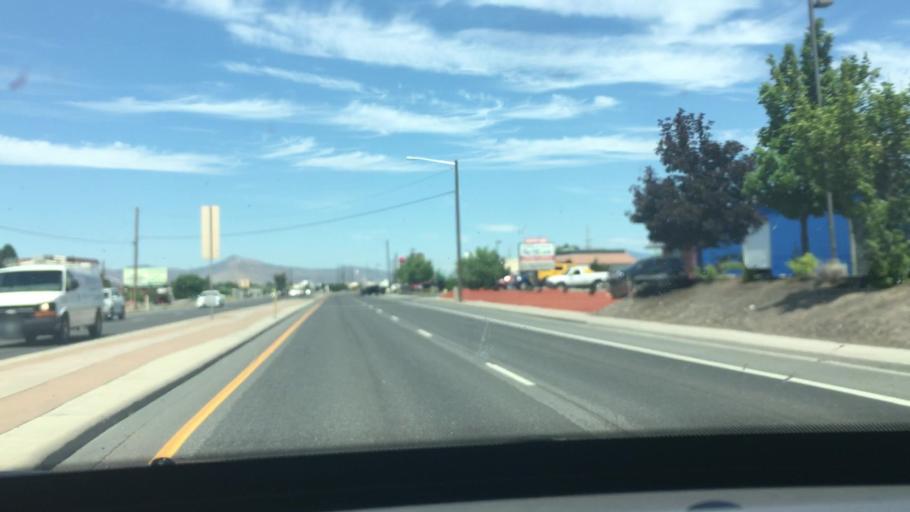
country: US
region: Oregon
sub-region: Deschutes County
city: Redmond
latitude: 44.2646
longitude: -121.1760
